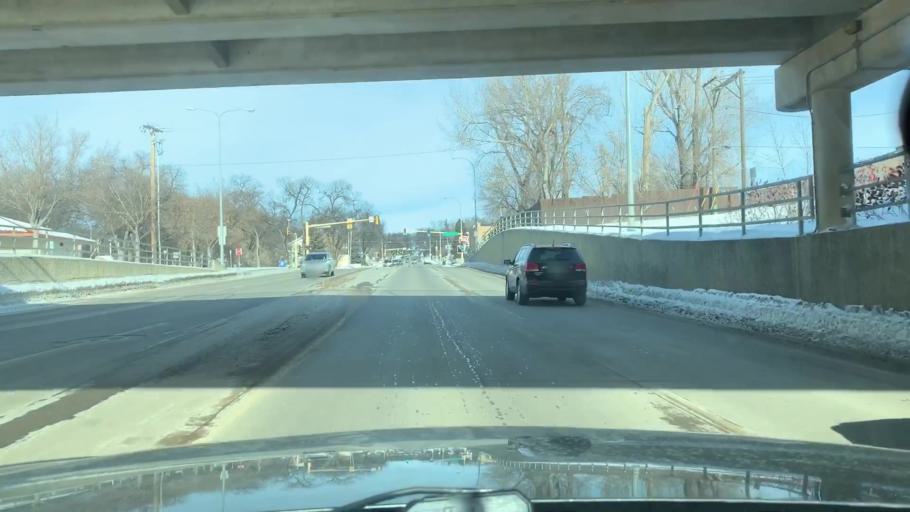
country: US
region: North Dakota
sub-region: Burleigh County
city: Bismarck
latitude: 46.8056
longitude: -100.7944
